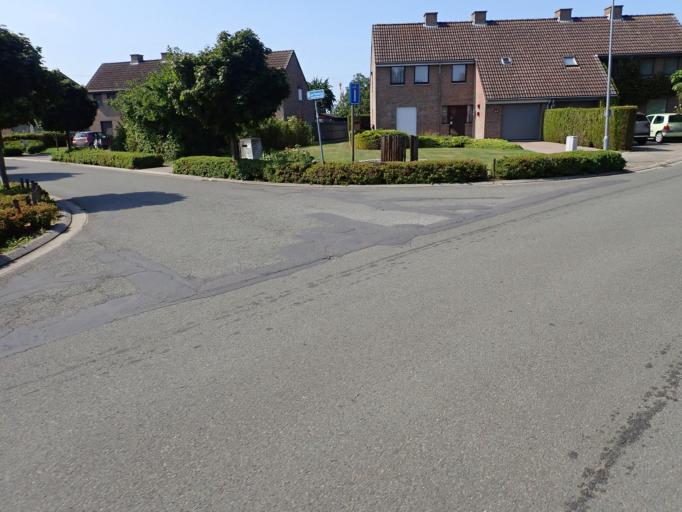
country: BE
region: Flanders
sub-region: Provincie Oost-Vlaanderen
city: Buggenhout
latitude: 51.0265
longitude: 4.1839
